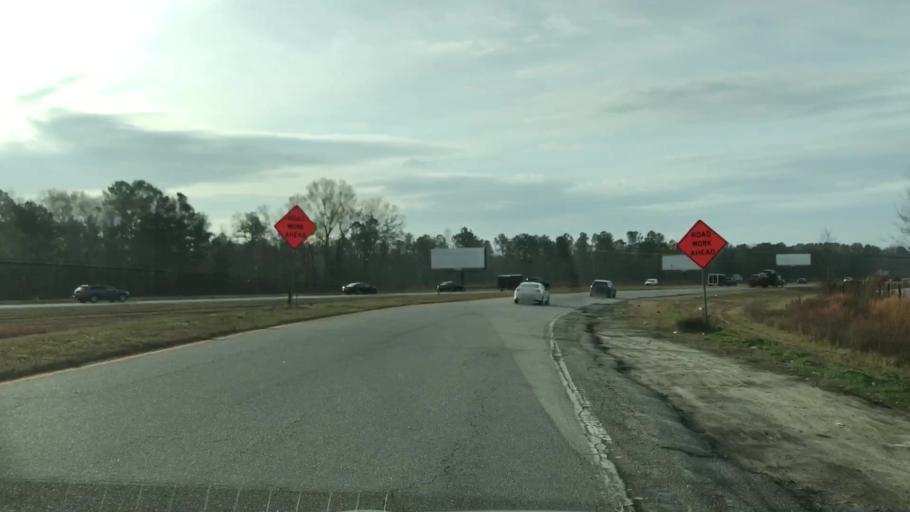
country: US
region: South Carolina
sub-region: Hampton County
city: Yemassee
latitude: 32.6281
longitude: -80.8846
